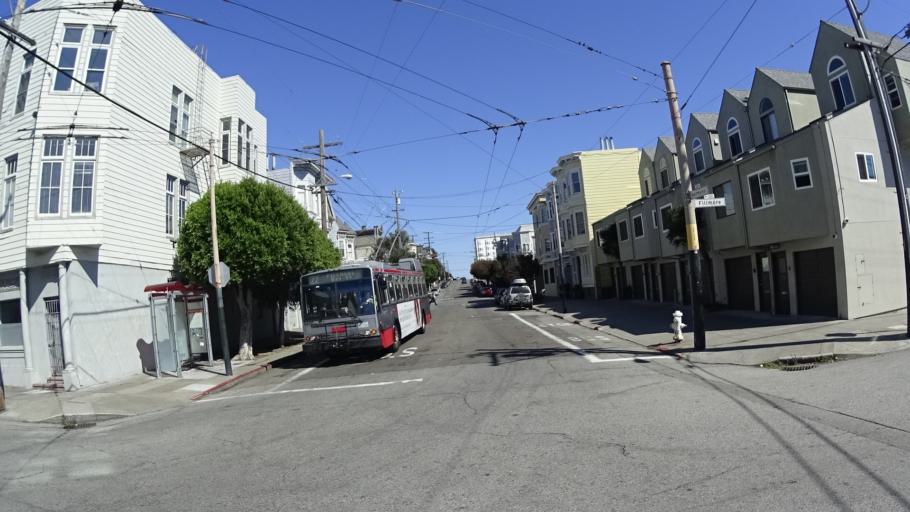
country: US
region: California
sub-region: San Francisco County
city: San Francisco
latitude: 37.7703
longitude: -122.4301
